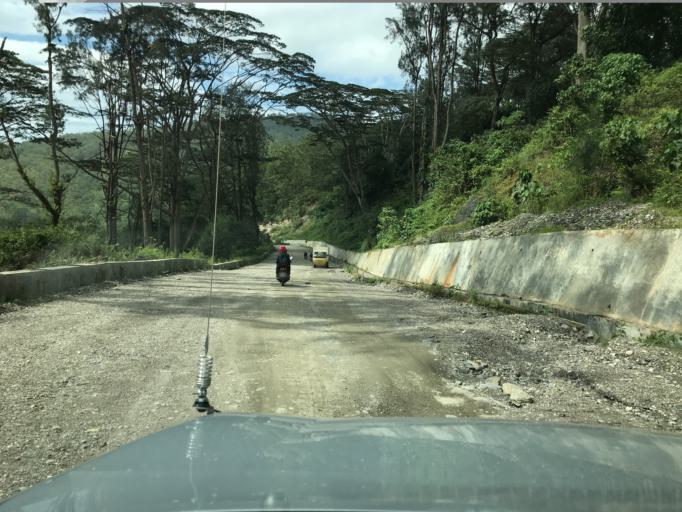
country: TL
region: Aileu
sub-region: Aileu Villa
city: Aileu
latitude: -8.6686
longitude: 125.5538
